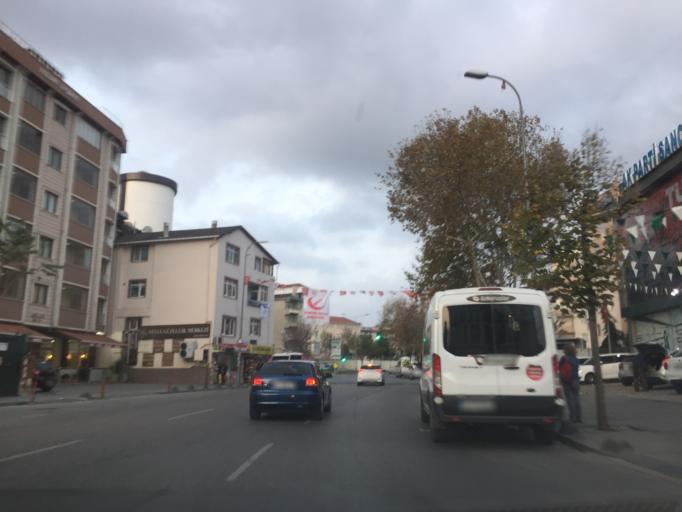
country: TR
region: Istanbul
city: Samandira
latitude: 40.9866
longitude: 29.2322
